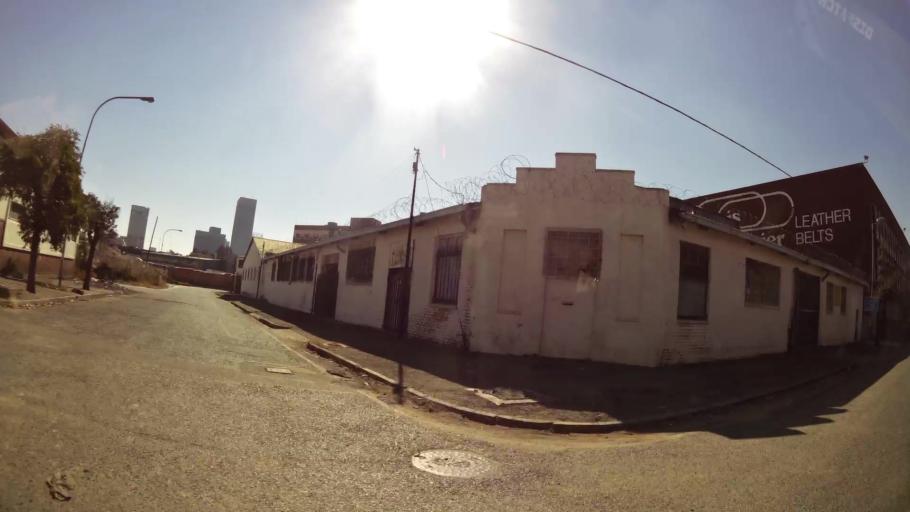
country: ZA
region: Gauteng
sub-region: City of Johannesburg Metropolitan Municipality
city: Johannesburg
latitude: -26.2150
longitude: 28.0472
